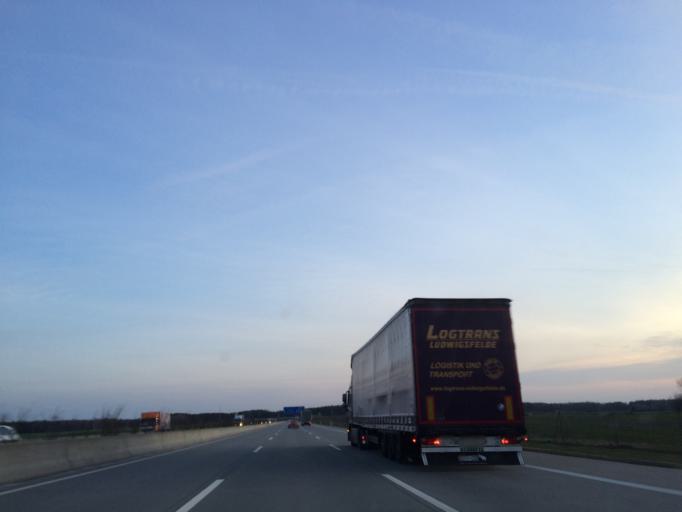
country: DE
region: Thuringia
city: Schwarzbach
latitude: 50.7945
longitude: 11.8953
